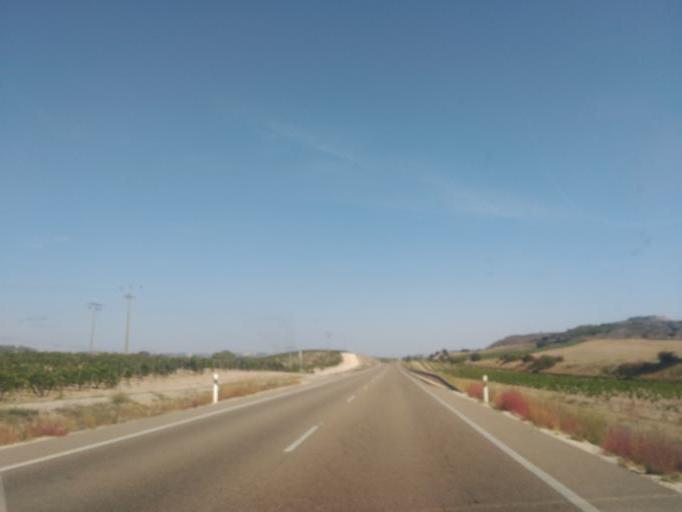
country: ES
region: Castille and Leon
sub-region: Provincia de Valladolid
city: Valbuena de Duero
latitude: 41.6240
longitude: -4.2660
